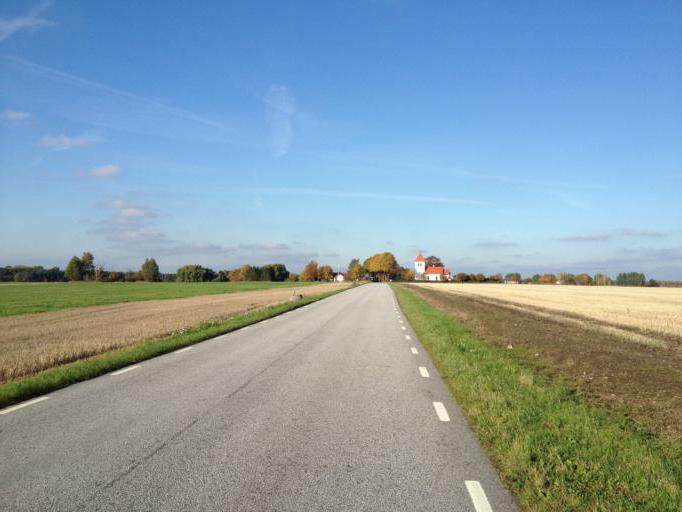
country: SE
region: Skane
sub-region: Kavlinge Kommun
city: Hofterup
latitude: 55.7808
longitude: 12.9754
